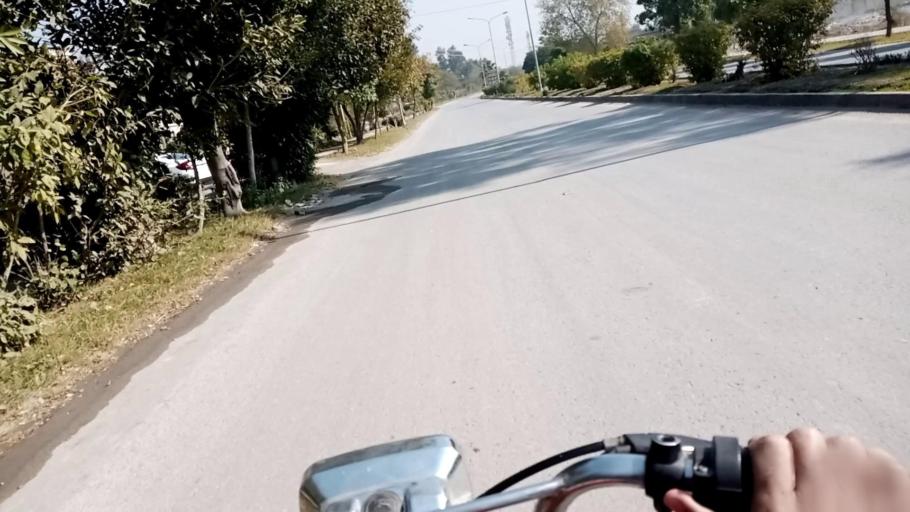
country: PK
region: Khyber Pakhtunkhwa
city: Peshawar
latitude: 33.9639
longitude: 71.4253
